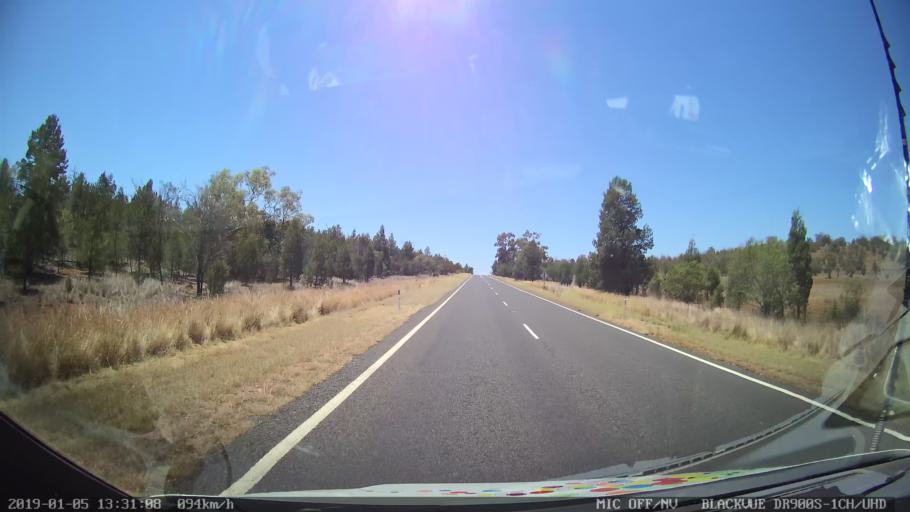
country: AU
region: New South Wales
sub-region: Gunnedah
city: Gunnedah
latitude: -31.0130
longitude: 150.0801
